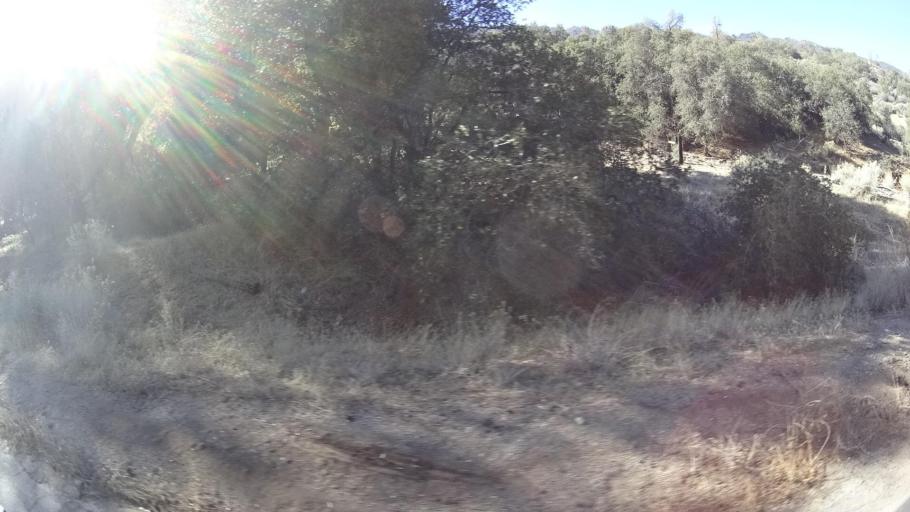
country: US
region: California
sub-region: Kern County
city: Bodfish
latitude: 35.4793
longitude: -118.5291
